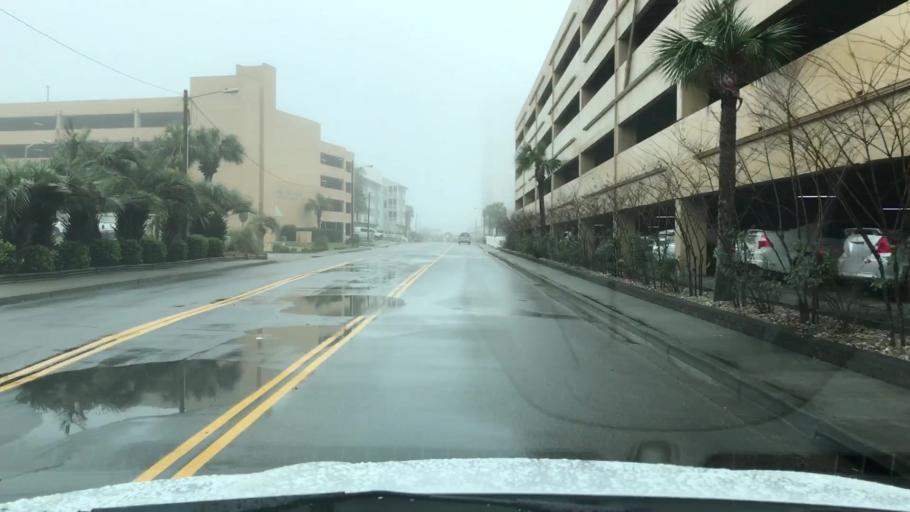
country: US
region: South Carolina
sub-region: Horry County
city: Myrtle Beach
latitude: 33.7599
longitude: -78.7902
